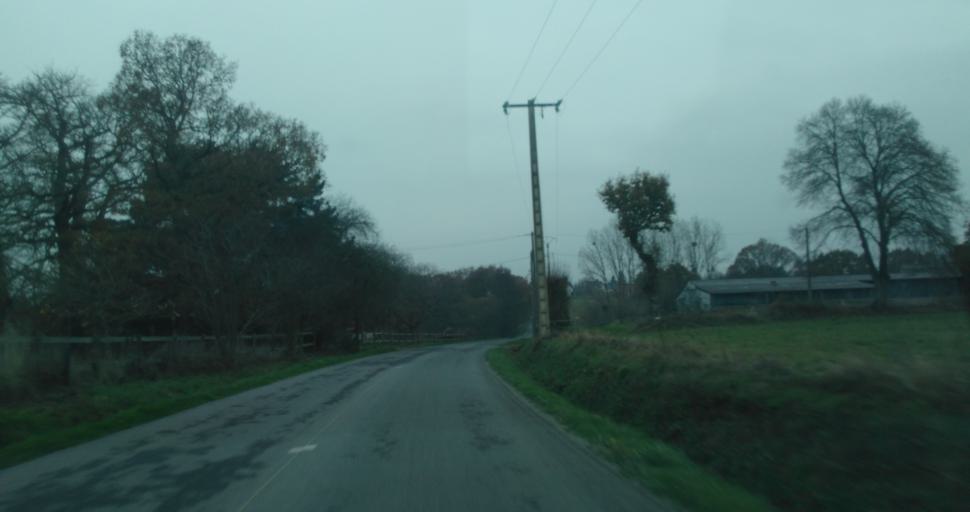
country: FR
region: Brittany
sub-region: Departement d'Ille-et-Vilaine
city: Iffendic
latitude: 48.0950
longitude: -2.1091
